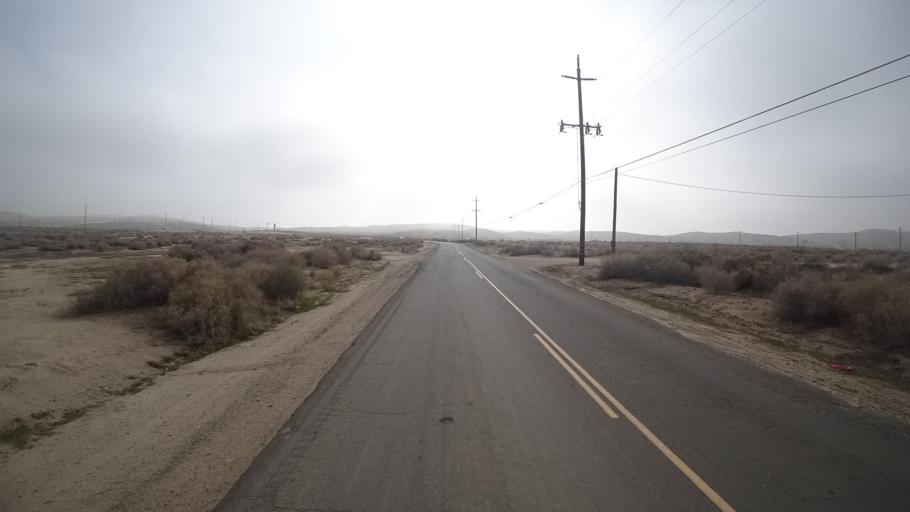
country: US
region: California
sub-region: Kern County
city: Ford City
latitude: 35.1803
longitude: -119.4291
